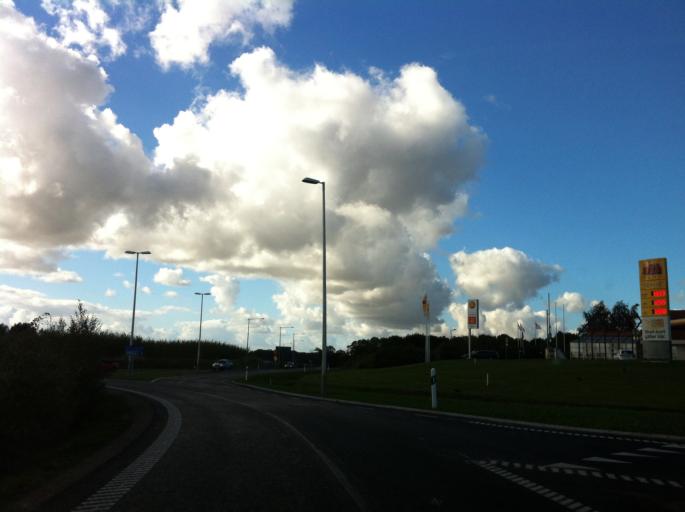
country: SE
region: Skane
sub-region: Eslovs Kommun
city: Eslov
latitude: 55.7695
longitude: 13.3201
